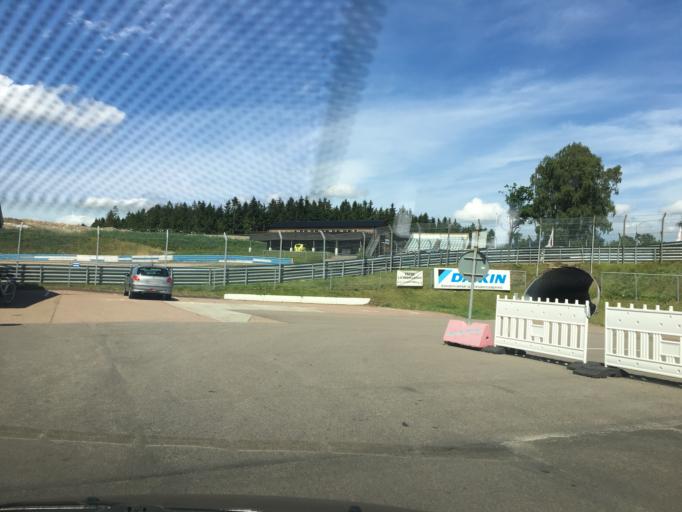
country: SE
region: Skane
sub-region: Svalovs Kommun
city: Kagerod
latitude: 55.9887
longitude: 13.1114
